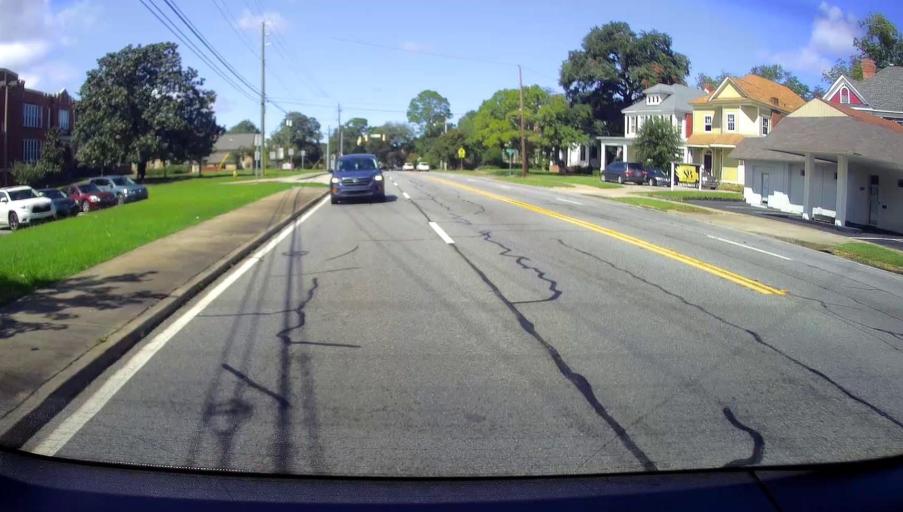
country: US
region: Georgia
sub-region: Bibb County
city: Macon
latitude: 32.8450
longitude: -83.6546
